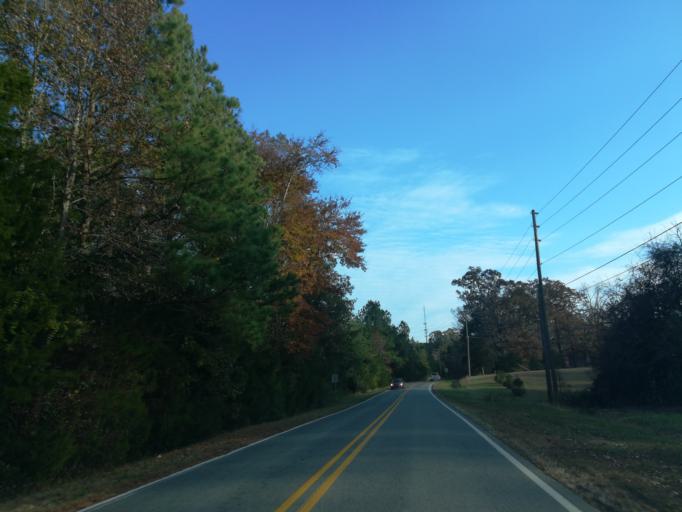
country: US
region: North Carolina
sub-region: Orange County
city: Chapel Hill
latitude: 35.9669
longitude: -79.0038
